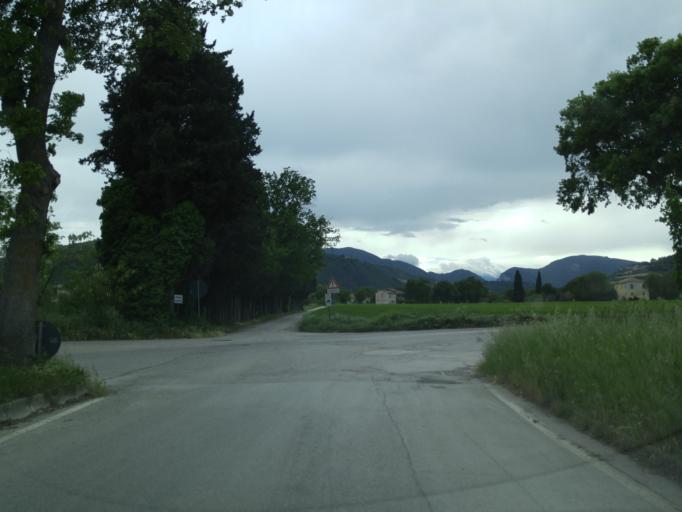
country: IT
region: The Marches
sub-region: Provincia di Pesaro e Urbino
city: Fossombrone
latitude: 43.7001
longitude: 12.8359
